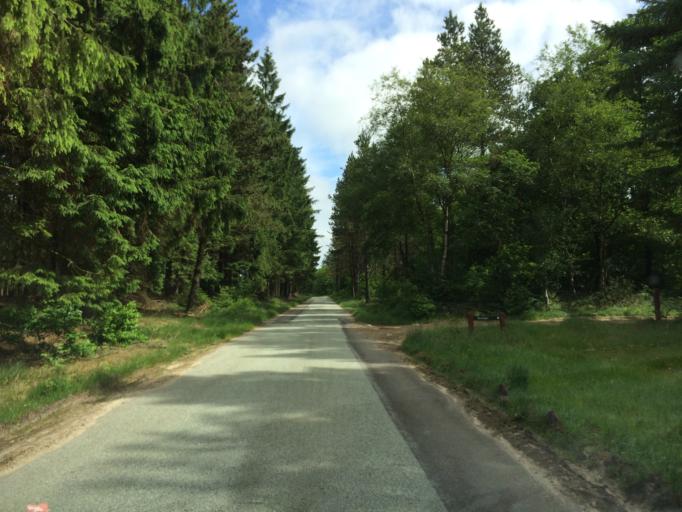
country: DK
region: Central Jutland
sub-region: Holstebro Kommune
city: Ulfborg
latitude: 56.2131
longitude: 8.4555
